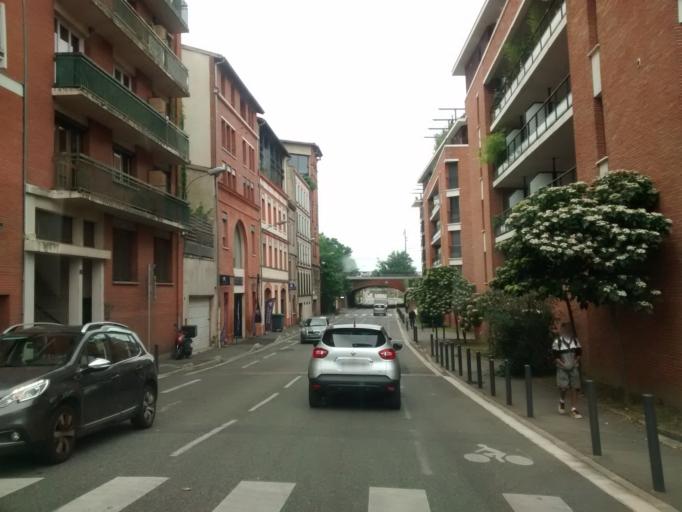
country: FR
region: Midi-Pyrenees
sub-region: Departement de la Haute-Garonne
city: Toulouse
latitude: 43.5932
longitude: 1.4429
